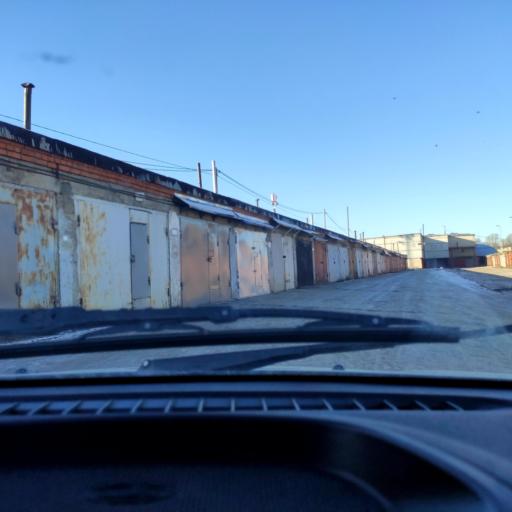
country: RU
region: Samara
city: Tol'yatti
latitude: 53.5138
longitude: 49.4362
